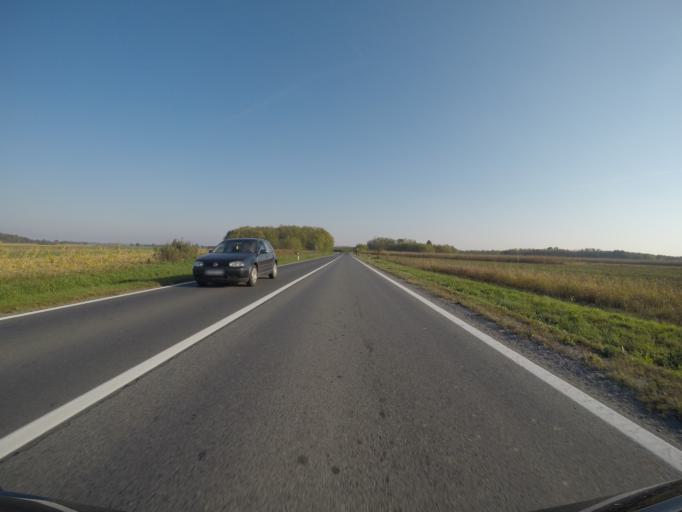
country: HR
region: Virovitick-Podravska
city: Pitomaca
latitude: 45.9740
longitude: 17.1734
